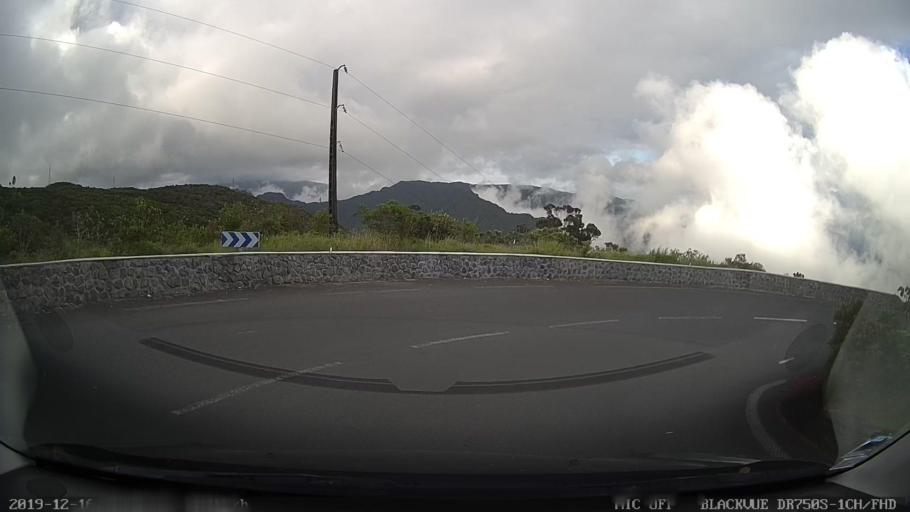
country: RE
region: Reunion
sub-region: Reunion
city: Cilaos
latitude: -21.1632
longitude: 55.5905
